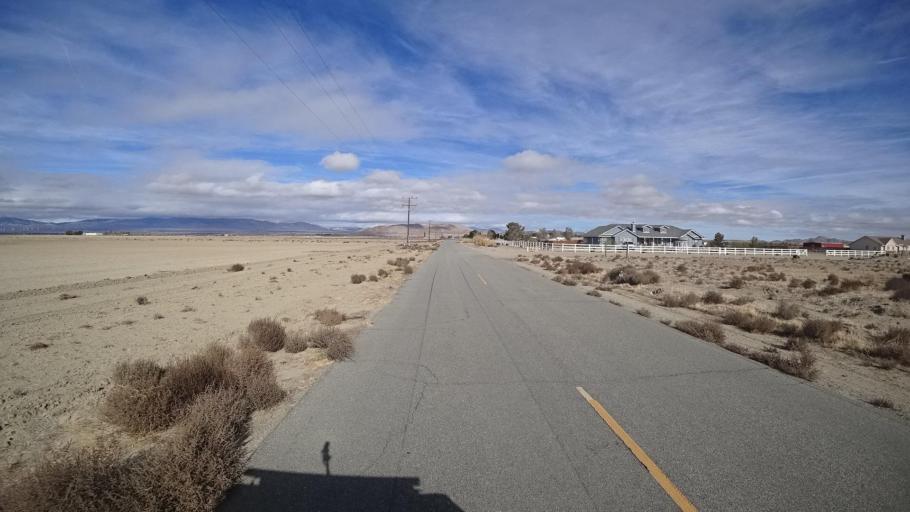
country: US
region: California
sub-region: Kern County
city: Rosamond
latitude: 34.8251
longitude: -118.2730
